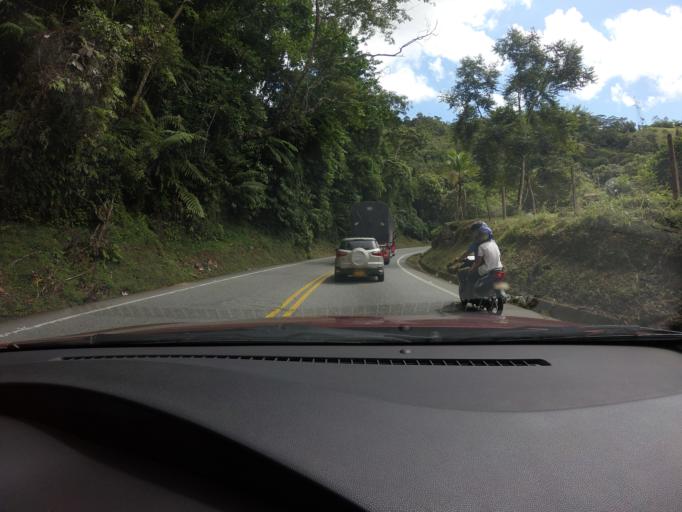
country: CO
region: Antioquia
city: San Luis
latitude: 5.9854
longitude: -74.9173
